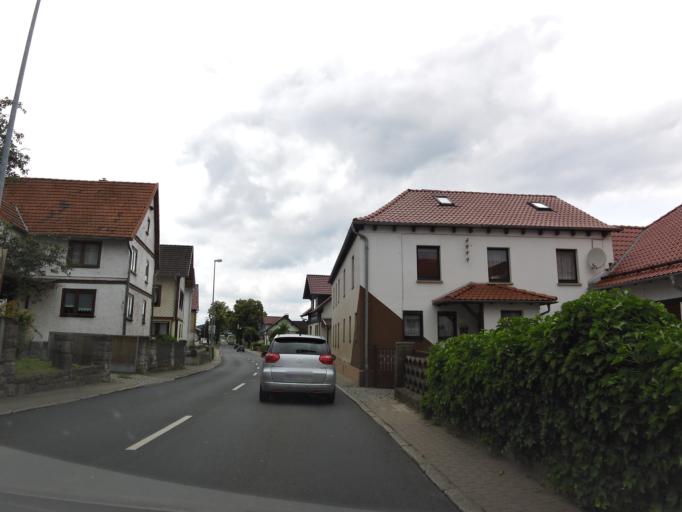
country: DE
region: Thuringia
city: Leimbach
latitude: 50.8217
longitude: 10.1804
